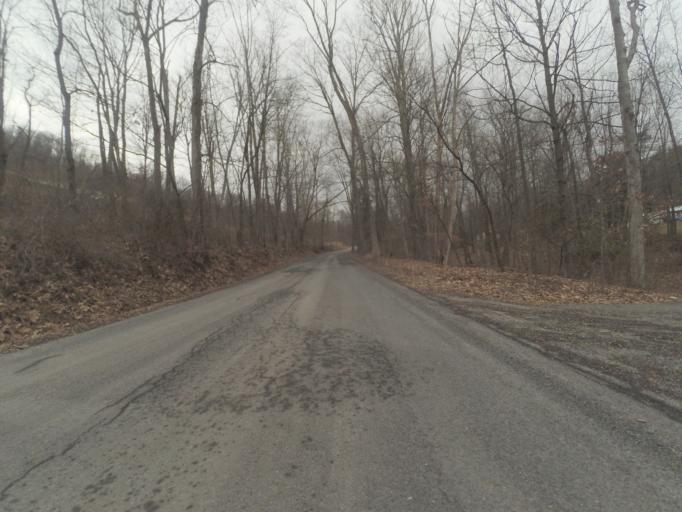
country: US
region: Pennsylvania
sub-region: Centre County
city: Stormstown
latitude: 40.8682
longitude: -78.0075
